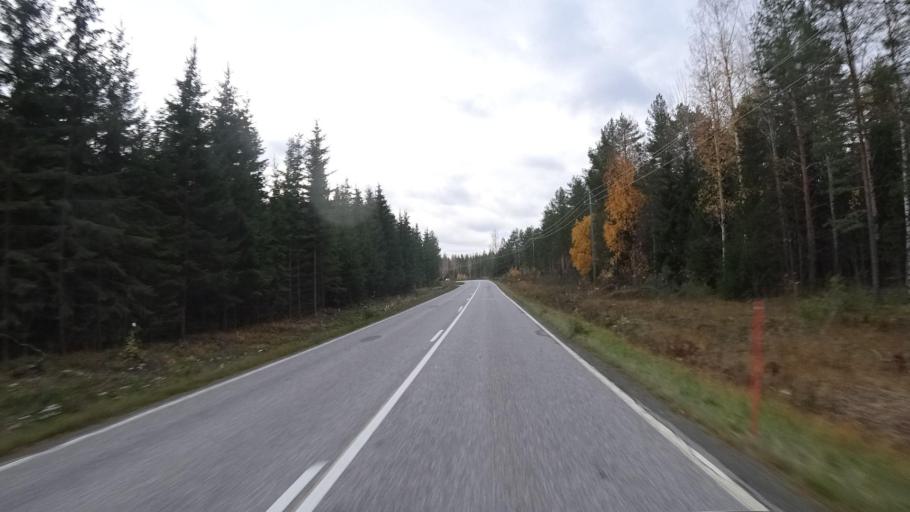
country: FI
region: Central Finland
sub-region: Joutsa
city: Joutsa
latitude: 61.7720
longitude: 26.1483
